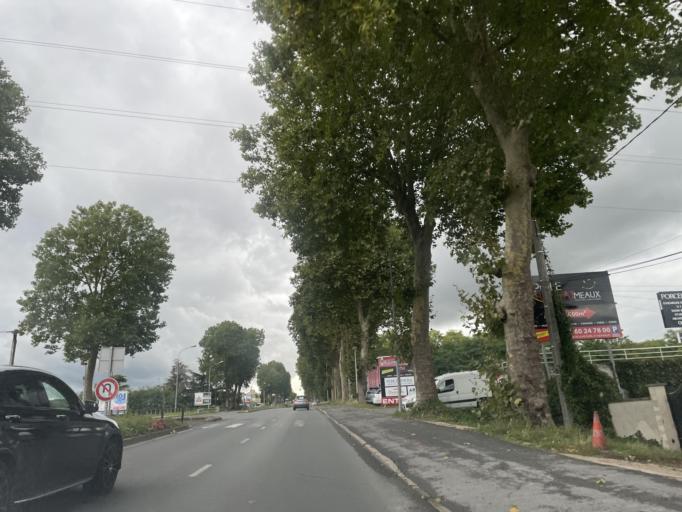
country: FR
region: Ile-de-France
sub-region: Departement de Seine-et-Marne
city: Fublaines
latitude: 48.9573
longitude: 2.9293
